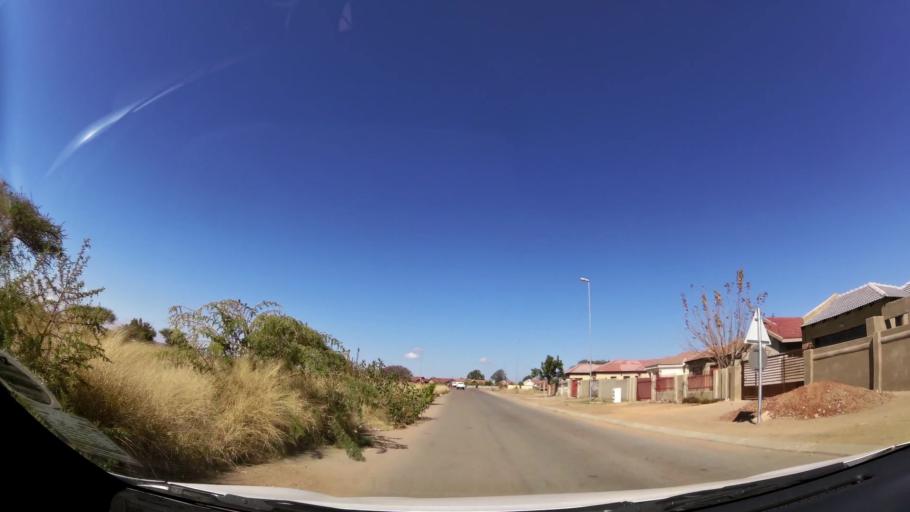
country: ZA
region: Limpopo
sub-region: Capricorn District Municipality
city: Polokwane
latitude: -23.8655
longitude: 29.4272
